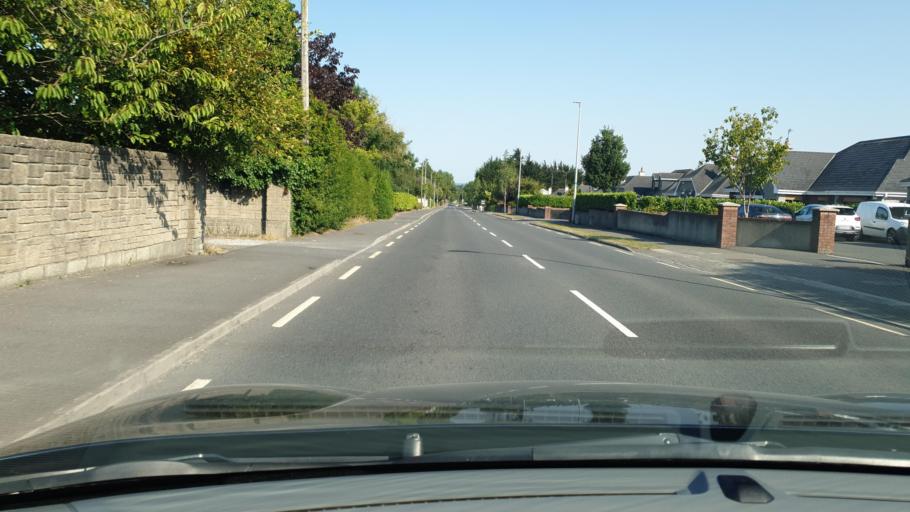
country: IE
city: Kentstown
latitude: 53.6284
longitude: -6.5387
